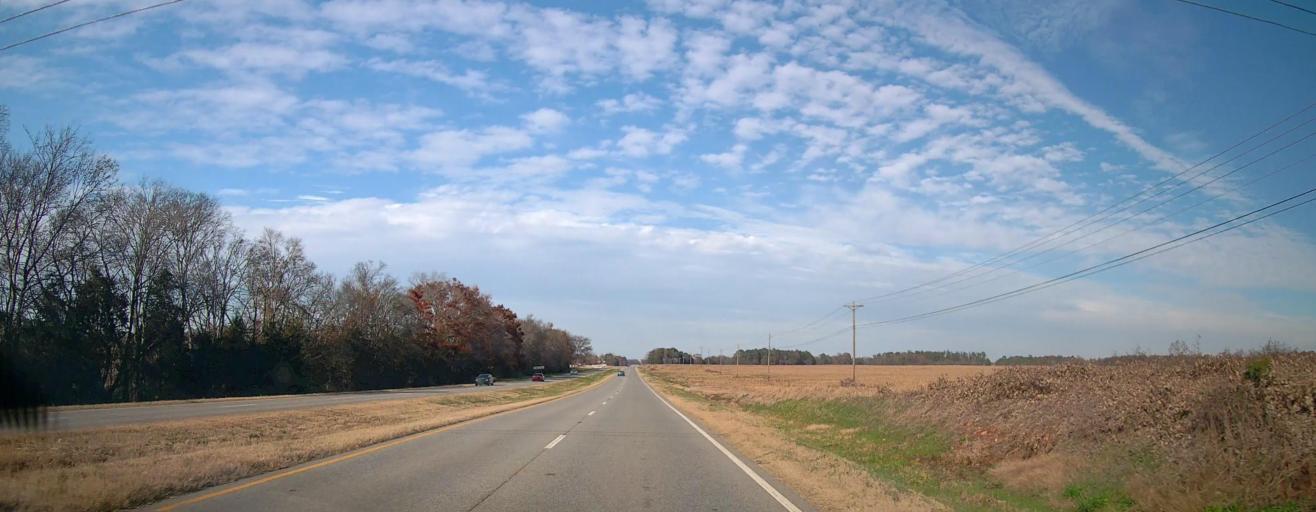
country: US
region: Alabama
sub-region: Morgan County
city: Decatur
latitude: 34.6611
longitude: -86.9501
